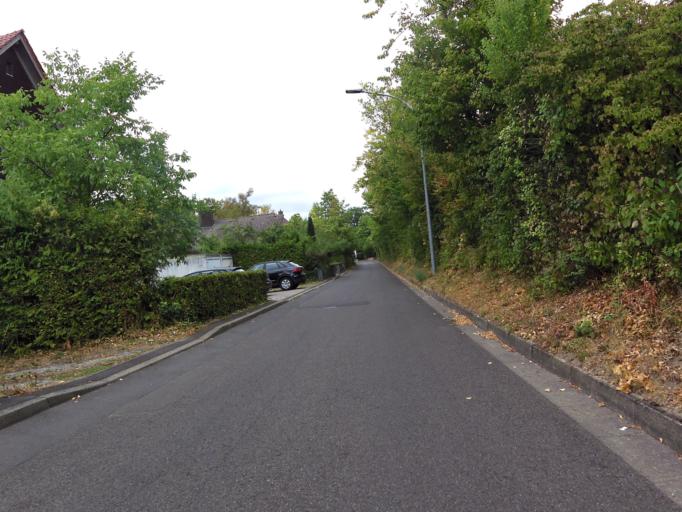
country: DE
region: Bavaria
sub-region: Regierungsbezirk Unterfranken
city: Veitshochheim
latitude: 49.8264
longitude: 9.8784
